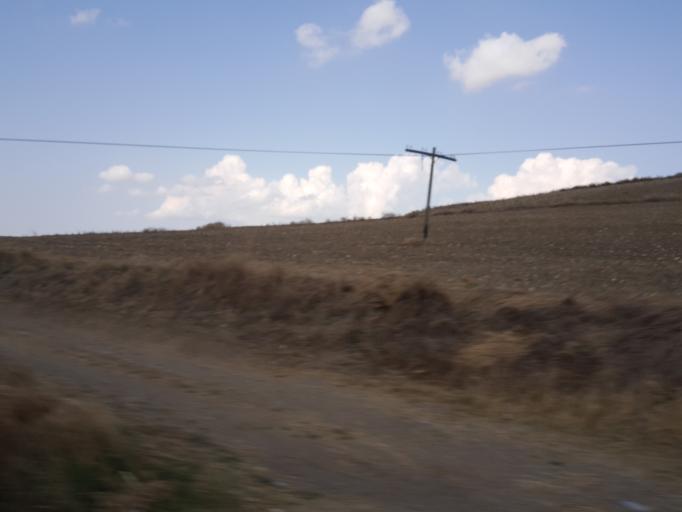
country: TR
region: Corum
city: Bogazkale
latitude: 40.1350
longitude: 34.5572
